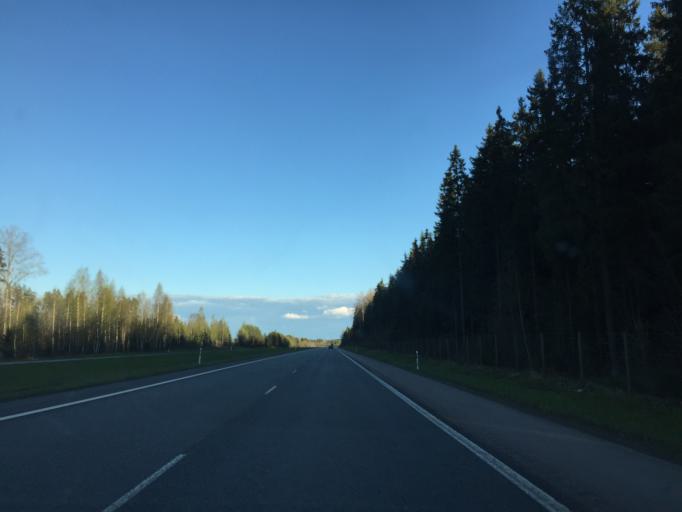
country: FI
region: Haeme
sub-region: Haemeenlinna
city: Tervakoski
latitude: 60.7920
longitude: 24.6941
